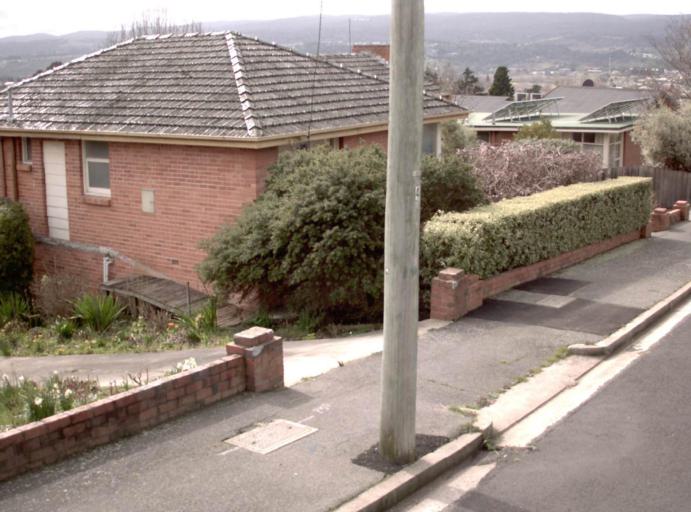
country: AU
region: Tasmania
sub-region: Launceston
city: East Launceston
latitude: -41.4534
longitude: 147.1572
